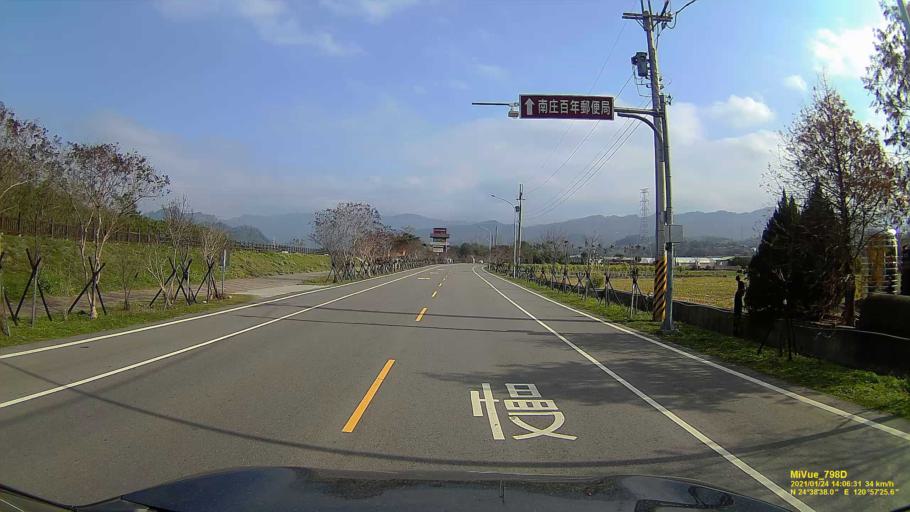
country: TW
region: Taiwan
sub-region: Miaoli
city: Miaoli
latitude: 24.6438
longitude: 120.9573
